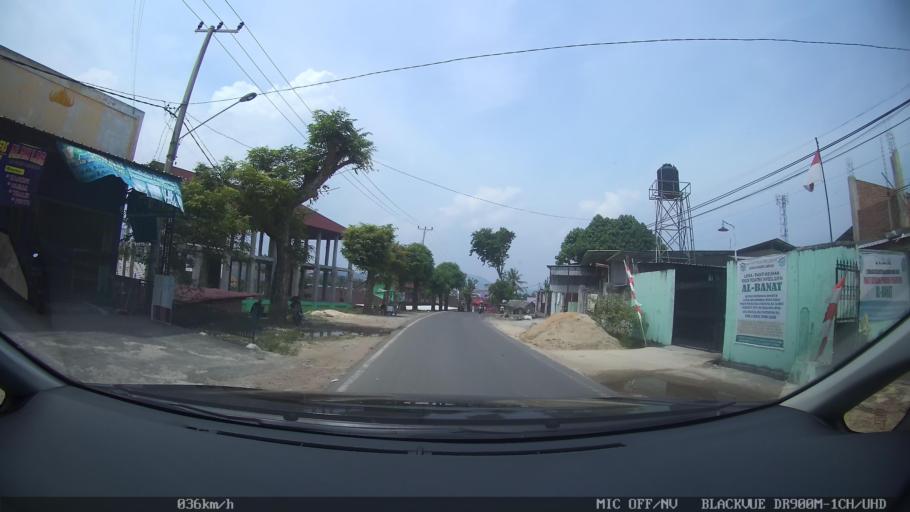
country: ID
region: Lampung
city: Bandarlampung
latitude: -5.4521
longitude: 105.2496
